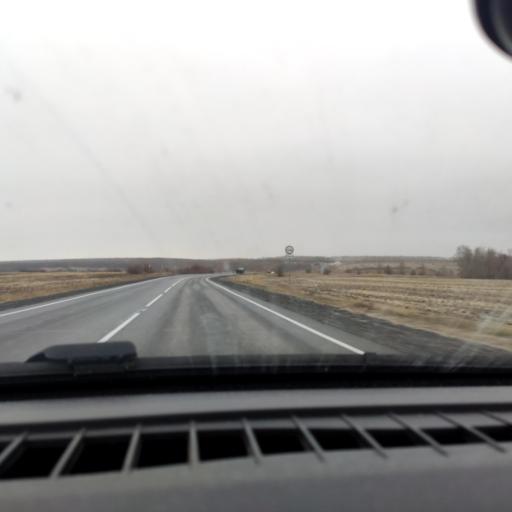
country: RU
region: Voronezj
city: Ostrogozhsk
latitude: 50.9267
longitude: 39.0581
